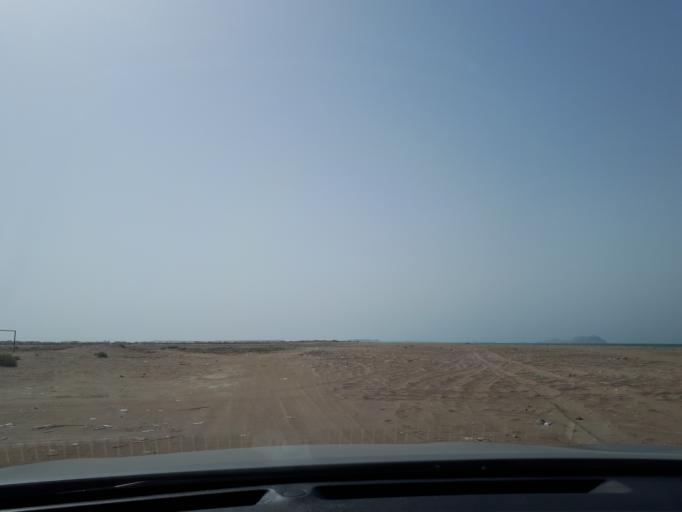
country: OM
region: Al Batinah
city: Barka'
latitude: 23.7317
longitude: 57.8347
